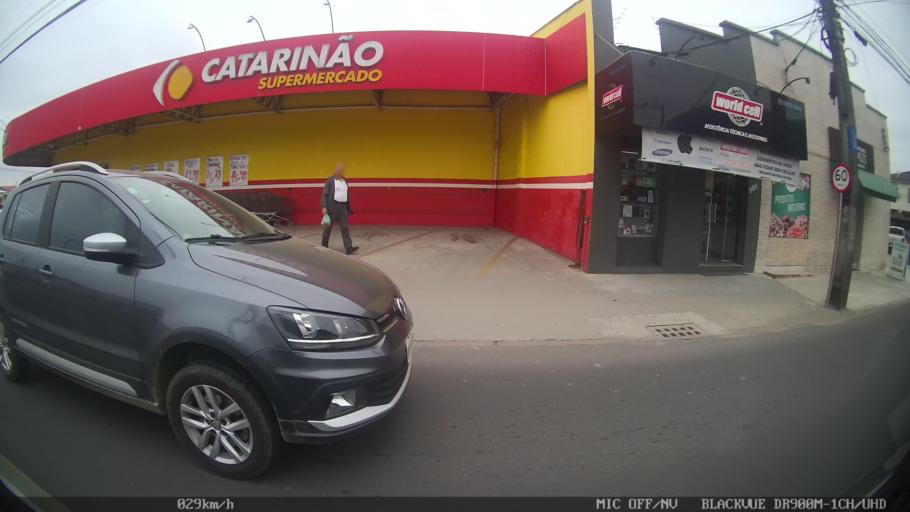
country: BR
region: Santa Catarina
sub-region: Joinville
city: Joinville
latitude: -26.3313
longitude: -48.8467
